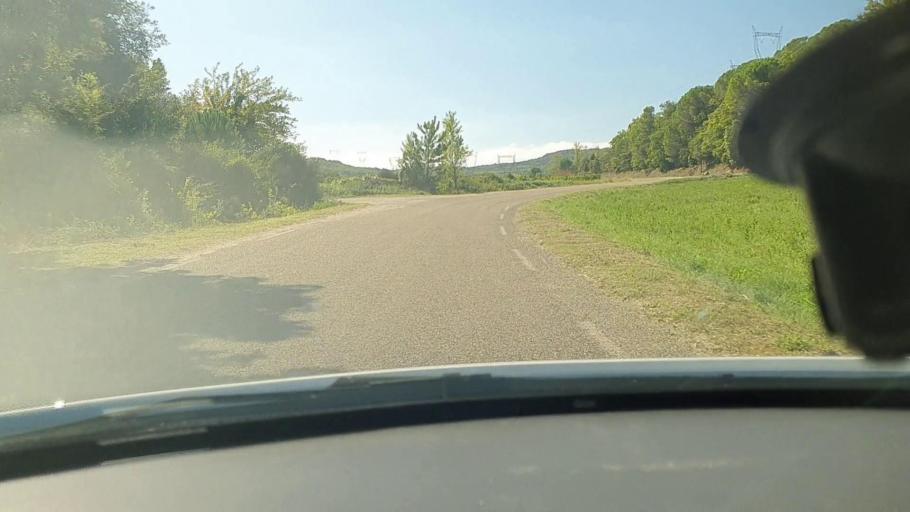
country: FR
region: Languedoc-Roussillon
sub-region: Departement du Gard
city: Saint-Paulet-de-Caisson
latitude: 44.2501
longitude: 4.5861
